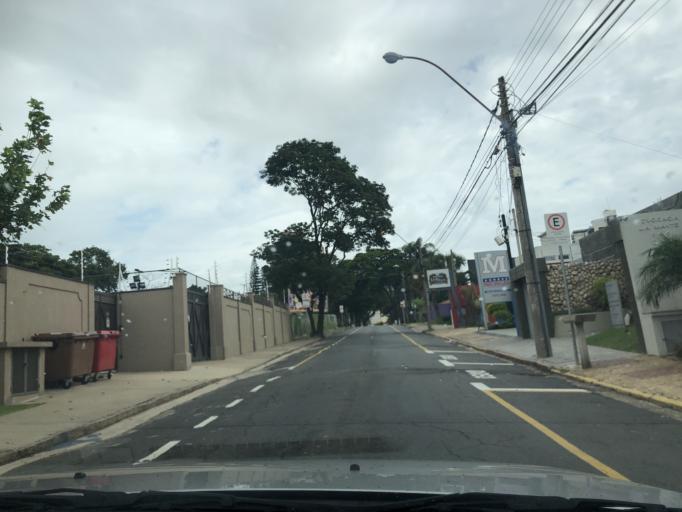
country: BR
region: Sao Paulo
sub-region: Americana
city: Americana
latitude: -22.7418
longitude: -47.3344
